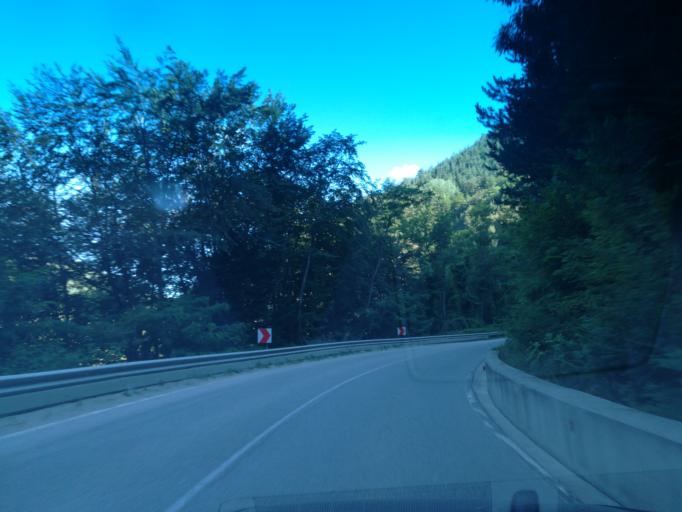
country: BG
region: Smolyan
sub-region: Obshtina Chepelare
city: Chepelare
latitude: 41.8233
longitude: 24.6919
